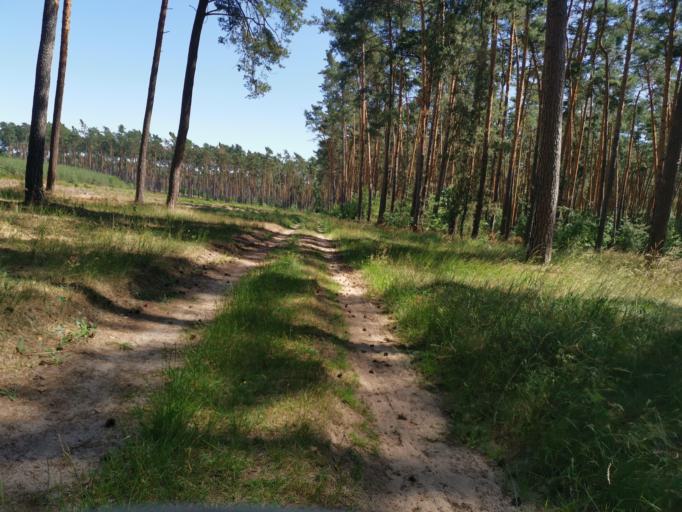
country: CZ
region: South Moravian
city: Rohatec
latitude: 48.9084
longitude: 17.2176
